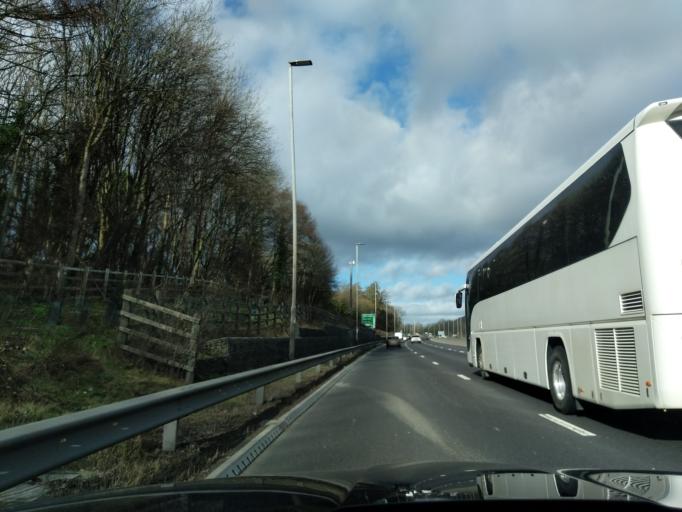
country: GB
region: England
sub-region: Gateshead
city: Lamesley
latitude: 54.9288
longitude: -1.6276
